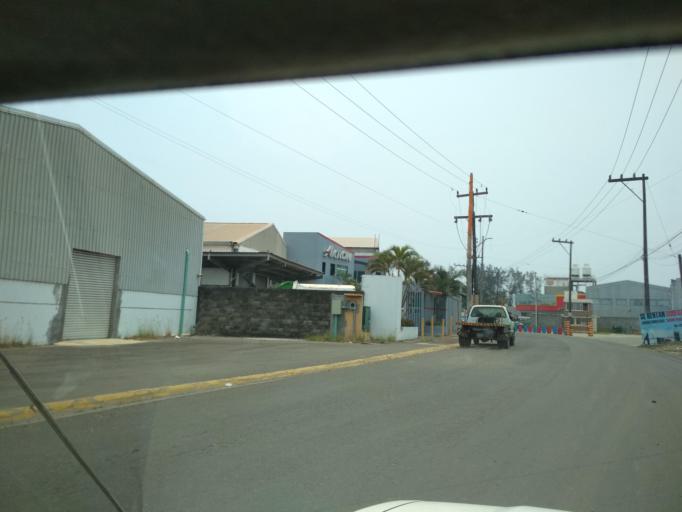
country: MX
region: Veracruz
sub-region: Veracruz
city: Lomas de Rio Medio Cuatro
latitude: 19.1685
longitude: -96.2391
